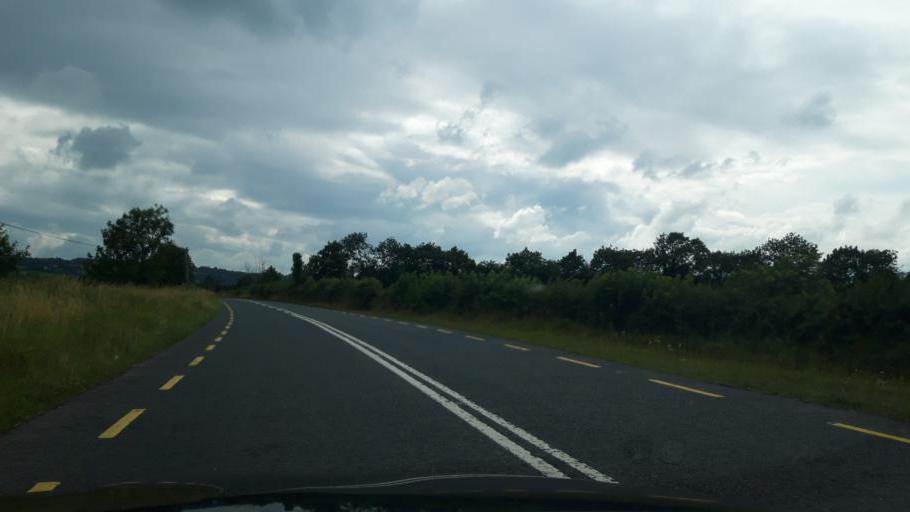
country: IE
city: Ballylinan
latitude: 52.9152
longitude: -7.0734
